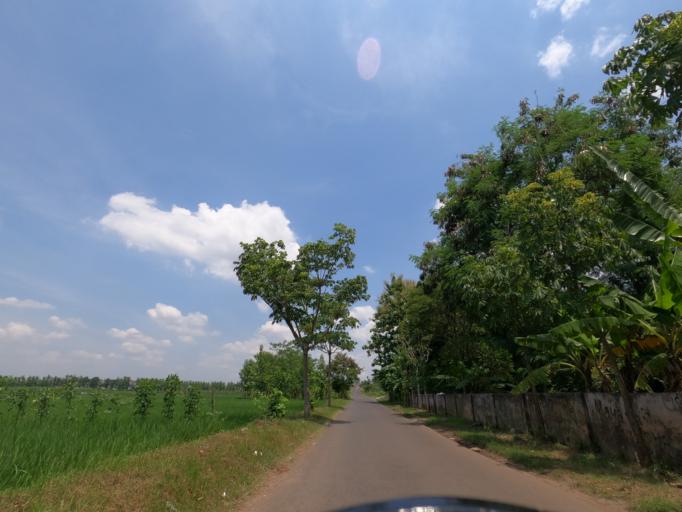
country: ID
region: West Java
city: Pamanukan
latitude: -6.5290
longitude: 107.7728
